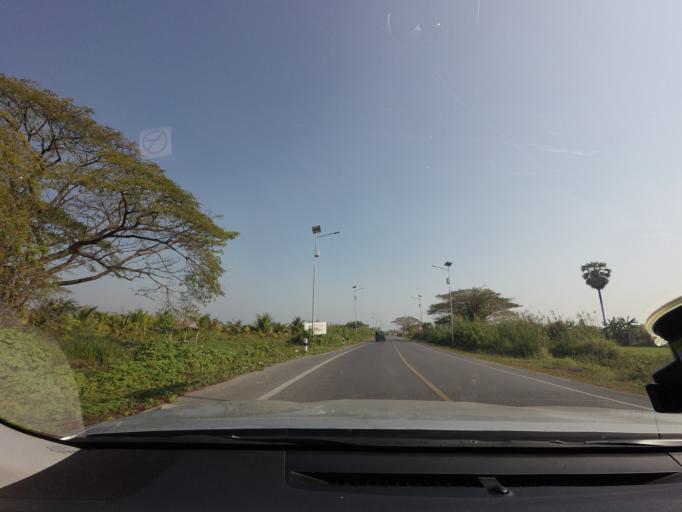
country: TH
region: Nakhon Si Thammarat
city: Nakhon Si Thammarat
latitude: 8.4629
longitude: 99.9793
